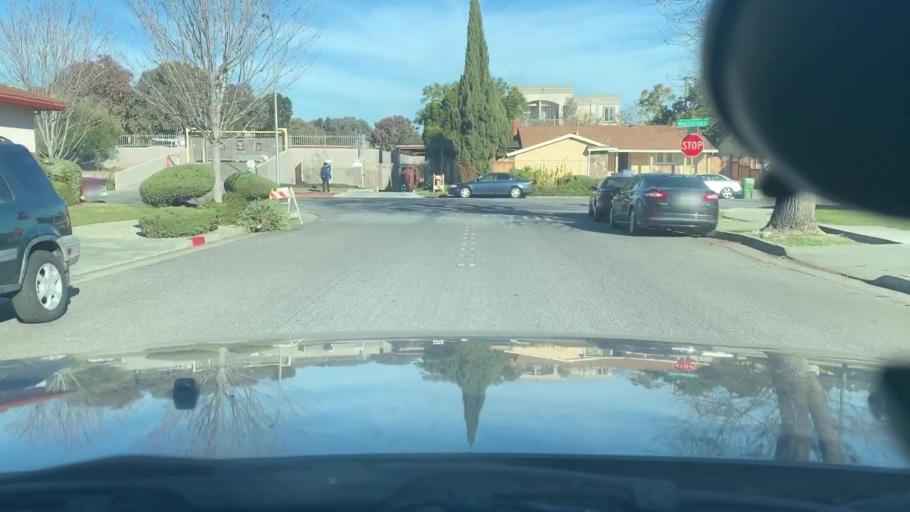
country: US
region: California
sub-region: Santa Clara County
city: Campbell
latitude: 37.3111
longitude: -121.9749
